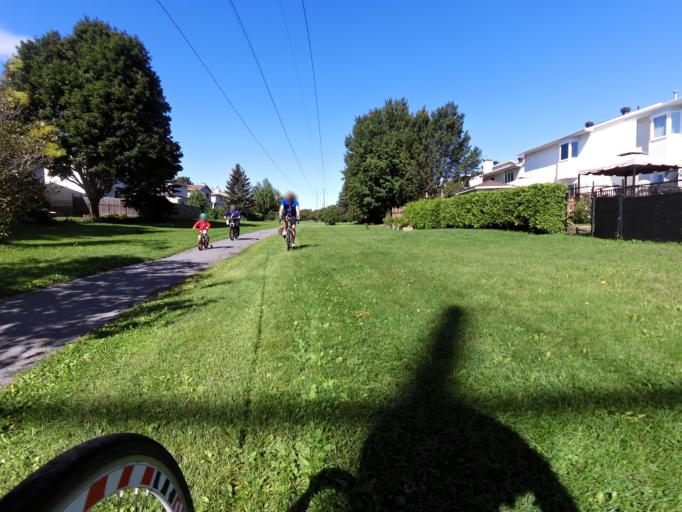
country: CA
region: Ontario
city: Bells Corners
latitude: 45.2966
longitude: -75.8629
